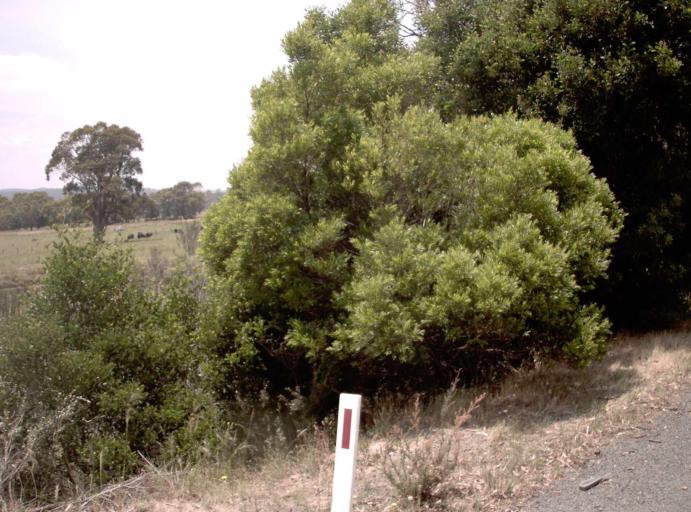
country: AU
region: Victoria
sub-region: Latrobe
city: Traralgon
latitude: -38.3805
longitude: 146.7586
